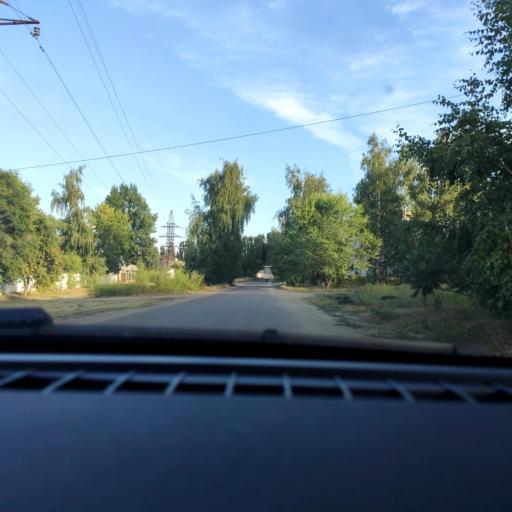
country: RU
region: Voronezj
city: Maslovka
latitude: 51.5795
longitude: 39.2980
